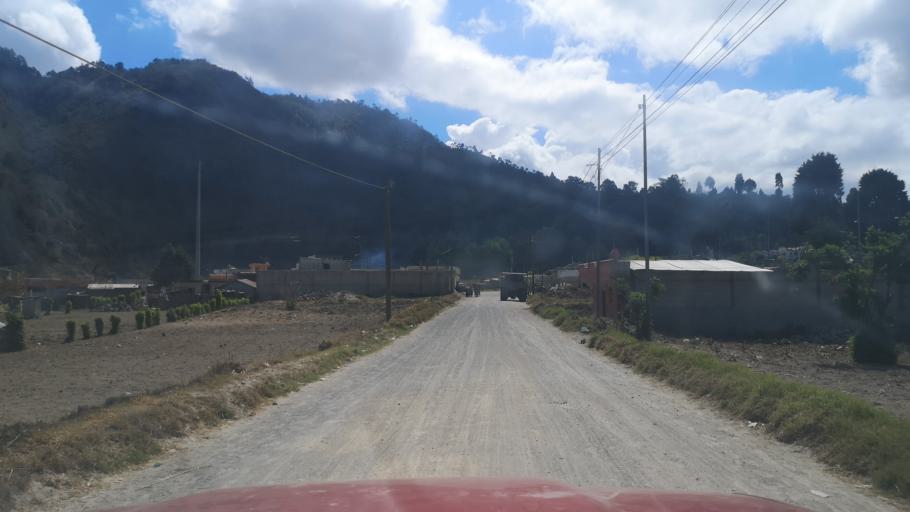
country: GT
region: Quetzaltenango
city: Almolonga
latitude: 14.7843
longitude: -91.5371
